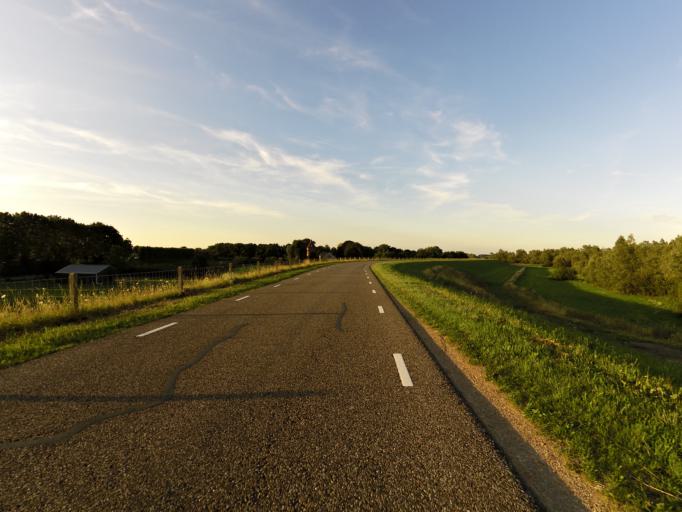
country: NL
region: Gelderland
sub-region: Gemeente Groesbeek
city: Berg en Dal
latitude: 51.8695
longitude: 5.9631
